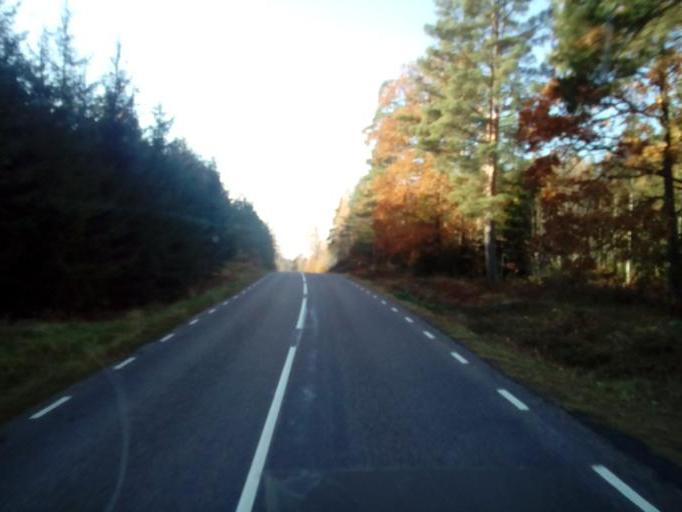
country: SE
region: Kalmar
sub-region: Vasterviks Kommun
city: Ankarsrum
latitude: 57.7868
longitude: 16.1748
